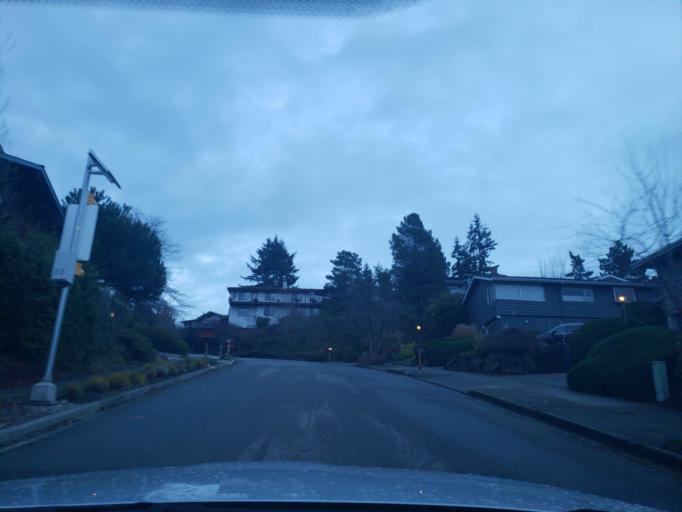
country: US
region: Washington
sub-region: Snohomish County
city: Esperance
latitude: 47.7717
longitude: -122.3705
